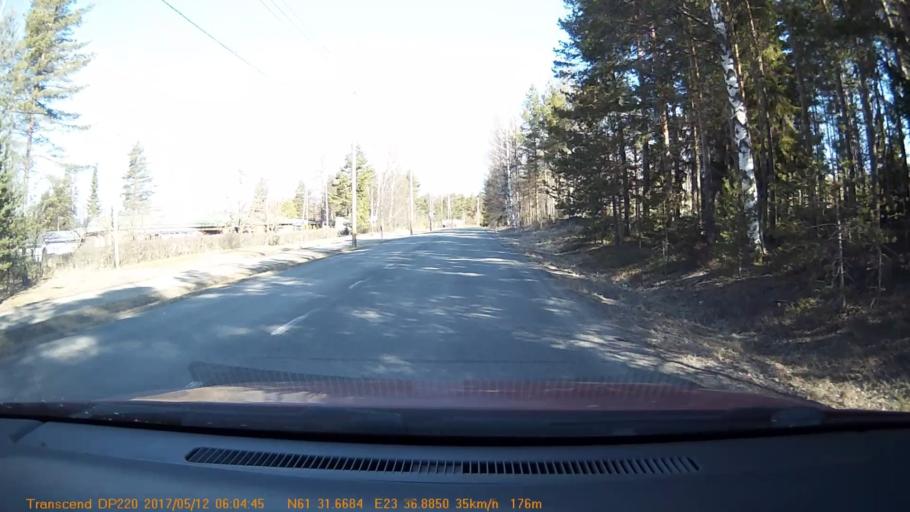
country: FI
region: Pirkanmaa
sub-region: Tampere
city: Yloejaervi
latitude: 61.5278
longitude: 23.6148
